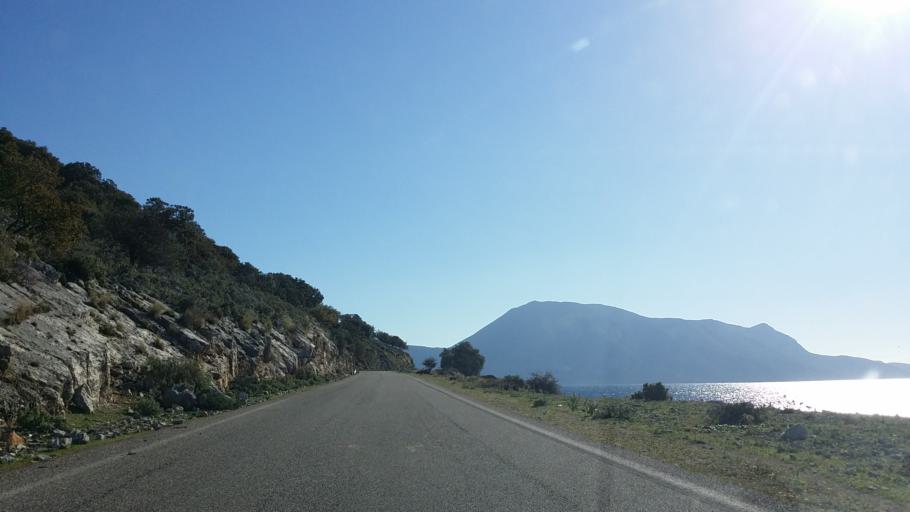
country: GR
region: West Greece
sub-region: Nomos Aitolias kai Akarnanias
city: Kandila
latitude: 38.7031
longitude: 20.8980
